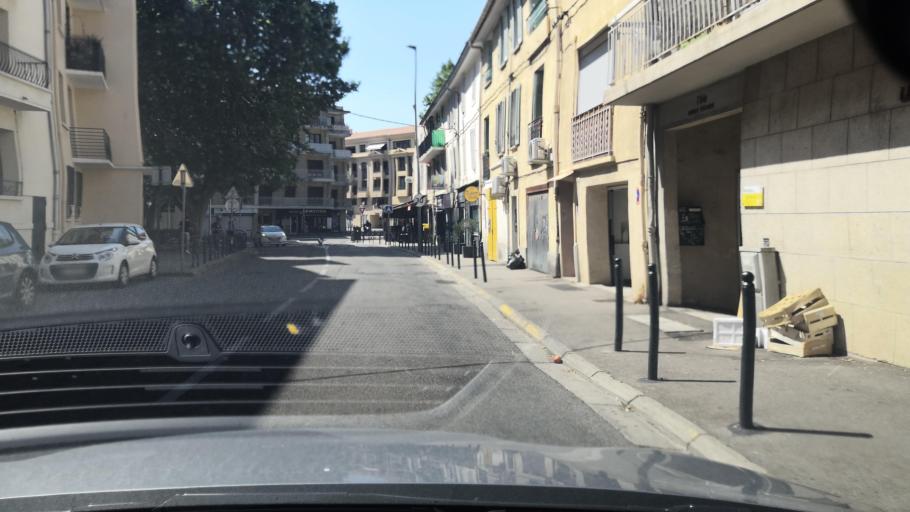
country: FR
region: Provence-Alpes-Cote d'Azur
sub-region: Departement des Bouches-du-Rhone
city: Aix-en-Provence
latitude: 43.5228
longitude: 5.4506
